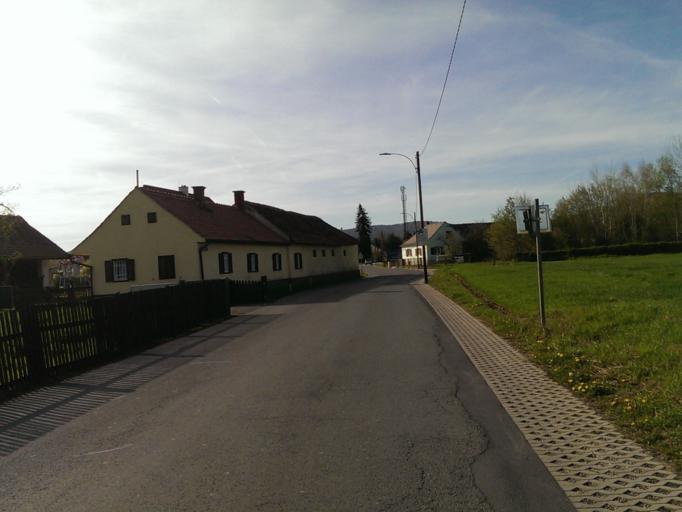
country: AT
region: Styria
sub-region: Politischer Bezirk Graz-Umgebung
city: Feldkirchen bei Graz
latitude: 47.0402
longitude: 15.4520
